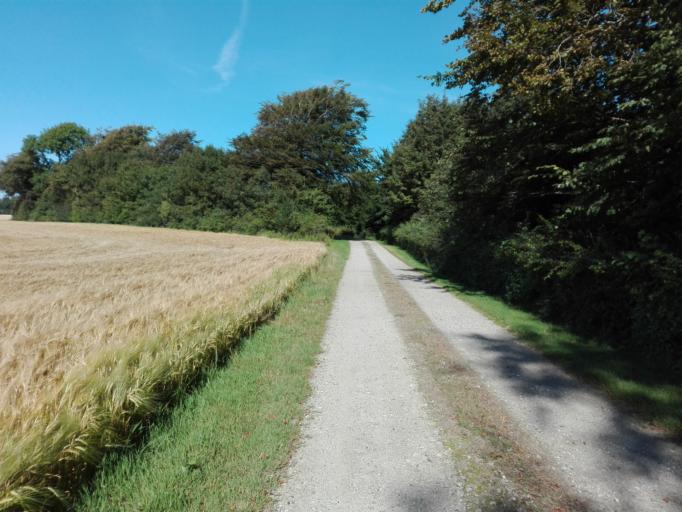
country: DK
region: Central Jutland
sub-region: Odder Kommune
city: Odder
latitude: 55.9538
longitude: 10.1032
